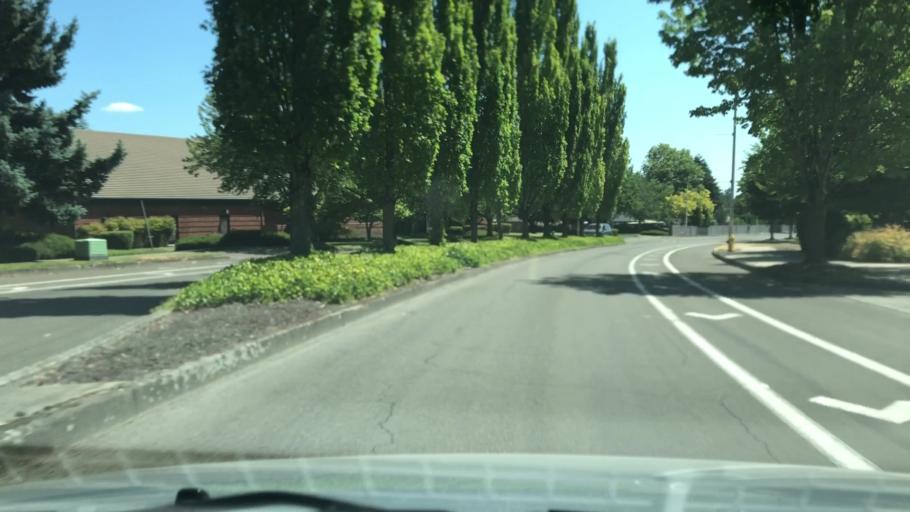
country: US
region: Oregon
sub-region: Clackamas County
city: Wilsonville
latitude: 45.3082
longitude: -122.7599
